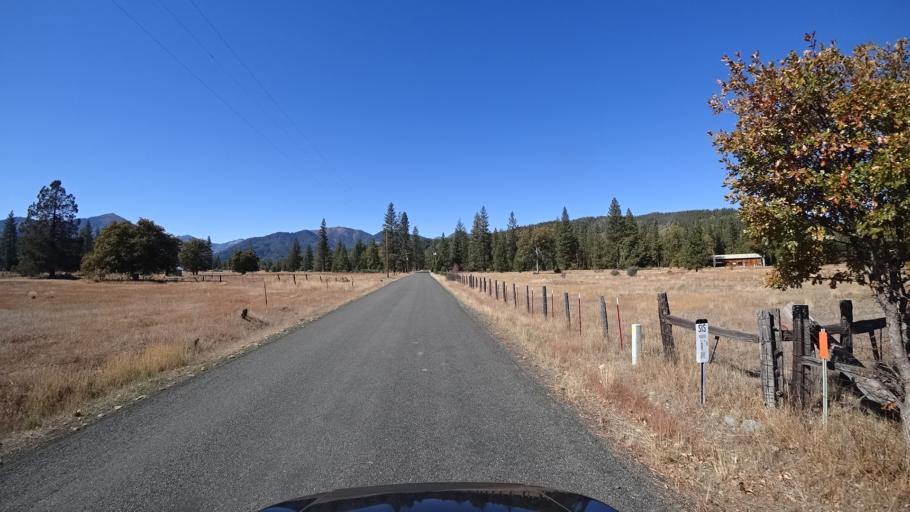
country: US
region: California
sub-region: Siskiyou County
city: Yreka
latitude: 41.5485
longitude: -122.9258
